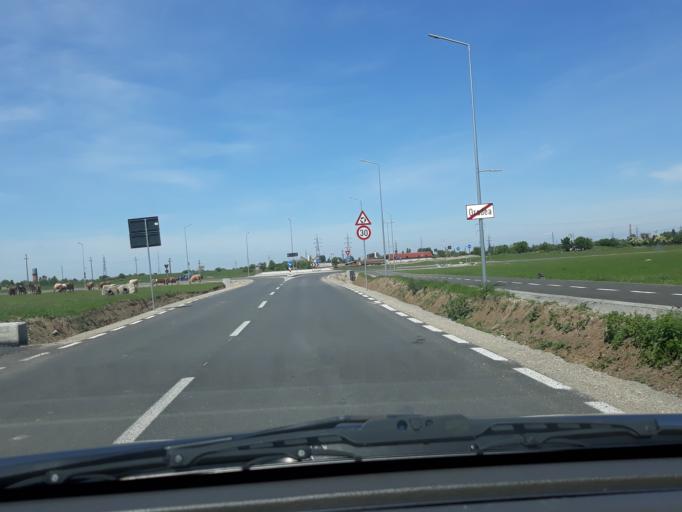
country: RO
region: Bihor
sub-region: Comuna Biharea
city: Oradea
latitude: 47.0698
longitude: 21.8993
